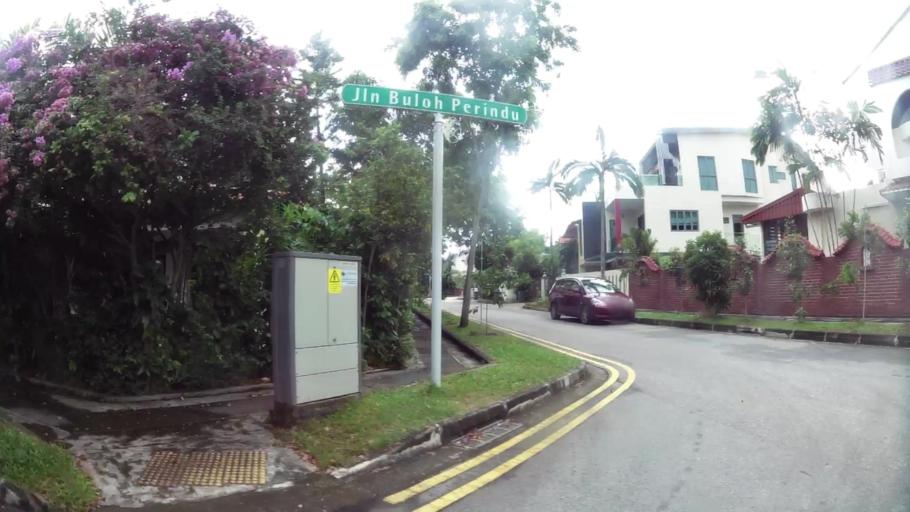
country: SG
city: Singapore
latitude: 1.3088
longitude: 103.9201
